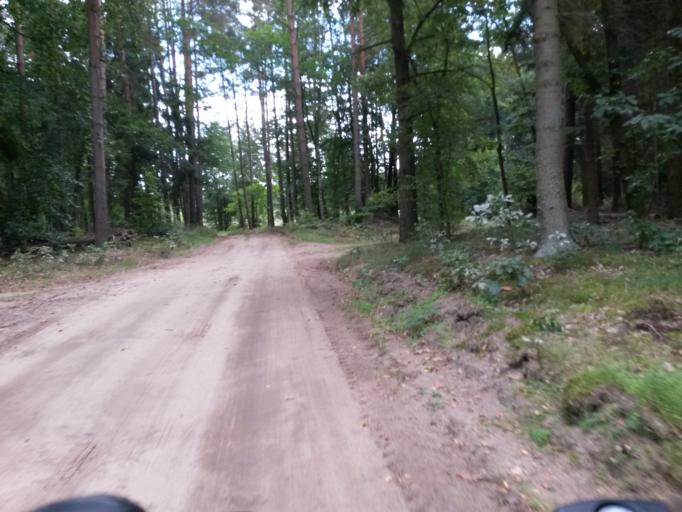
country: DE
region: Brandenburg
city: Templin
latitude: 53.1692
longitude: 13.4666
